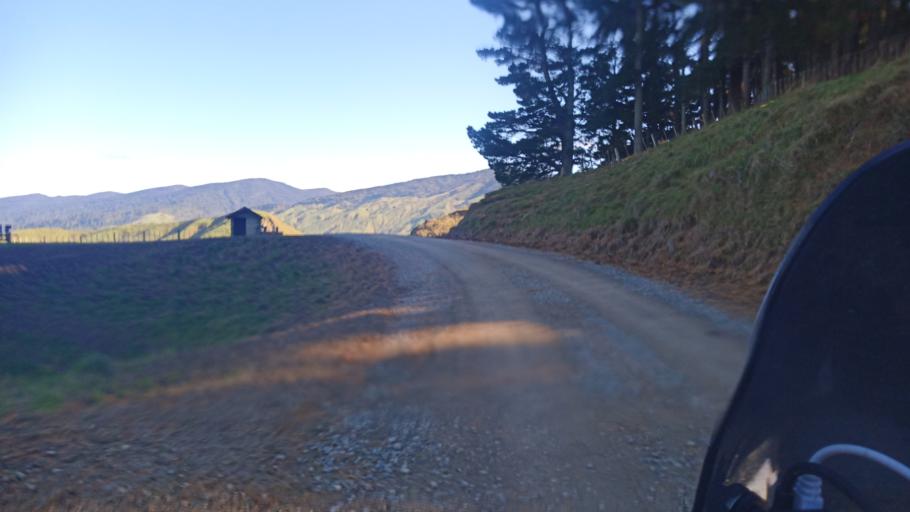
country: NZ
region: Hawke's Bay
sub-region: Wairoa District
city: Wairoa
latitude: -38.7861
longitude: 177.2714
